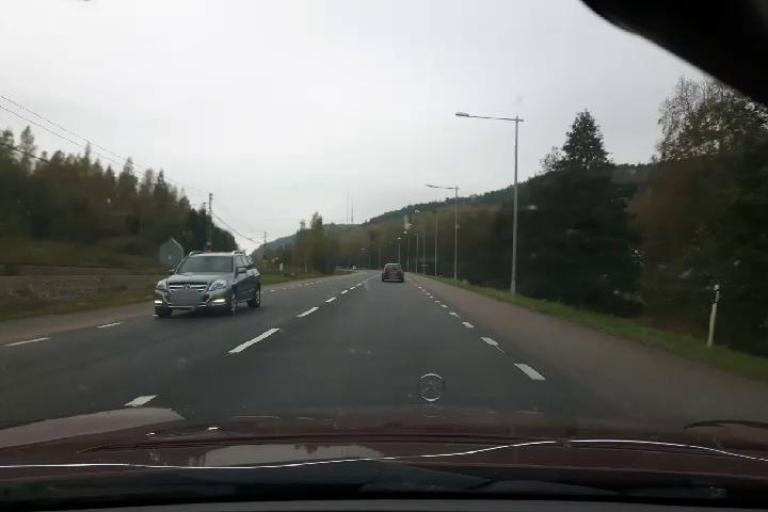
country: SE
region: Vaesternorrland
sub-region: OErnskoeldsviks Kommun
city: Ornskoldsvik
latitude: 63.2953
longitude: 18.6900
